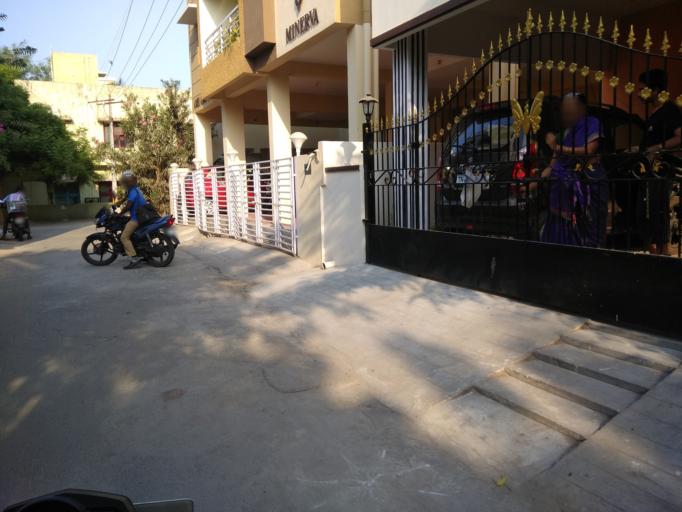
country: IN
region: Tamil Nadu
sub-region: Kancheepuram
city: Madipakkam
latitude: 12.9805
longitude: 80.1858
